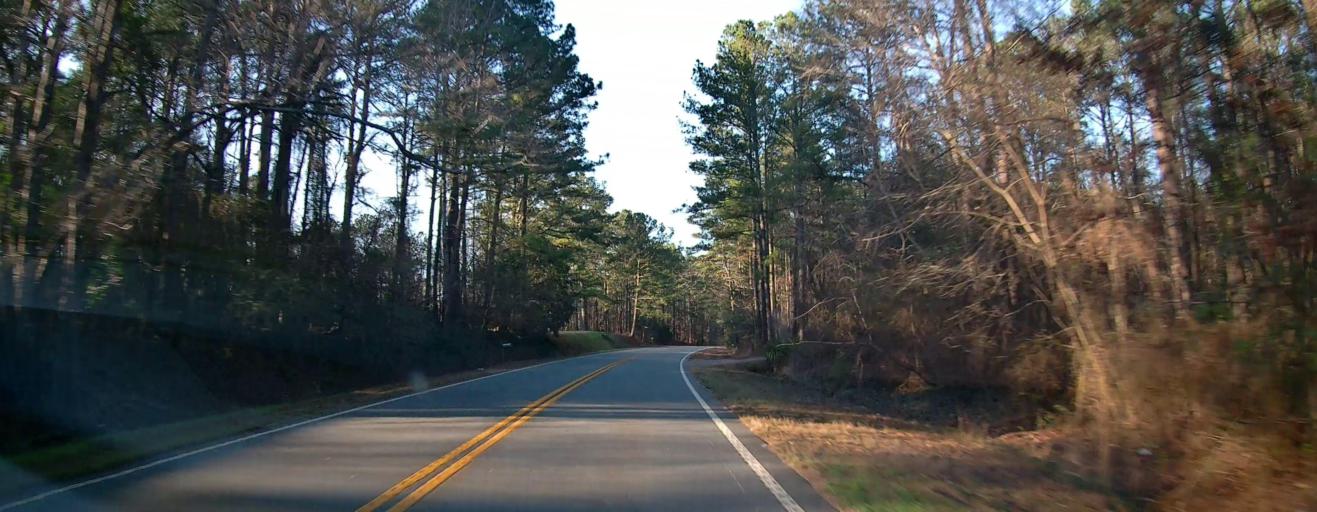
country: US
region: Alabama
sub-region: Chambers County
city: Valley
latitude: 32.7466
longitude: -85.0804
